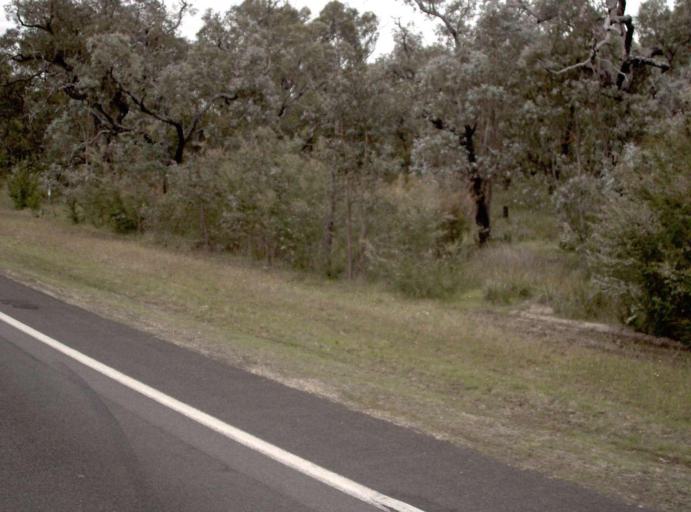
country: AU
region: Victoria
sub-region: Wellington
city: Sale
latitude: -38.3215
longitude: 147.0215
